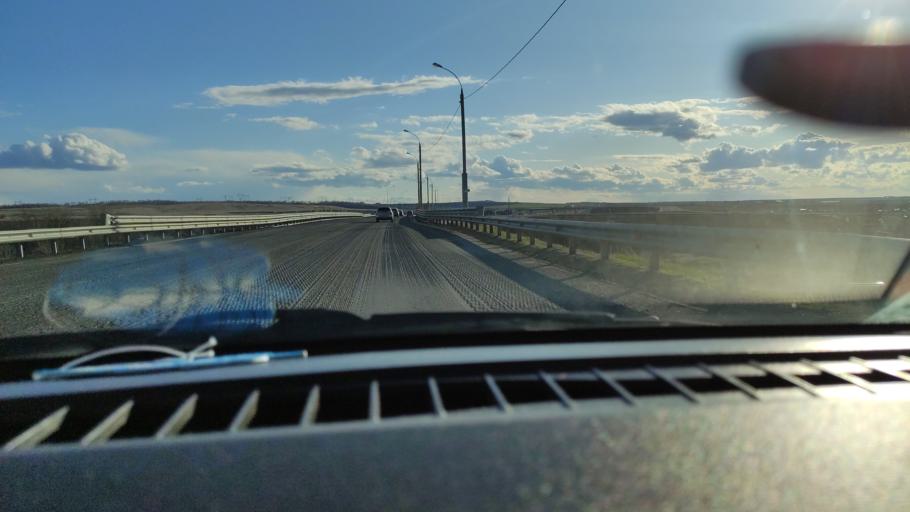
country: RU
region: Saratov
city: Yelshanka
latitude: 51.7992
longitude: 46.1833
